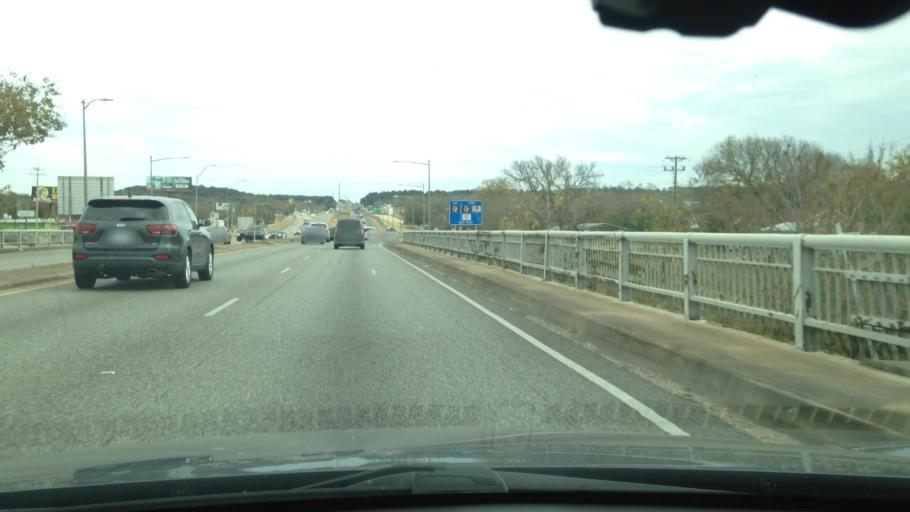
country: US
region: Texas
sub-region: Bastrop County
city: Bastrop
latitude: 30.1050
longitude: -97.3192
